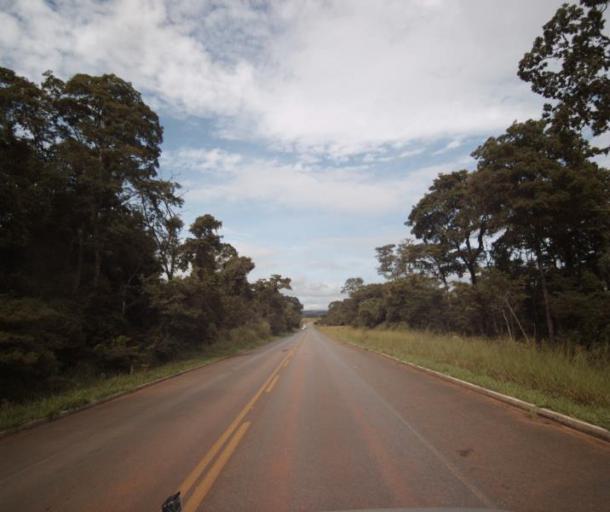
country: BR
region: Goias
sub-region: Pirenopolis
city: Pirenopolis
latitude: -15.6641
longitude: -48.6872
